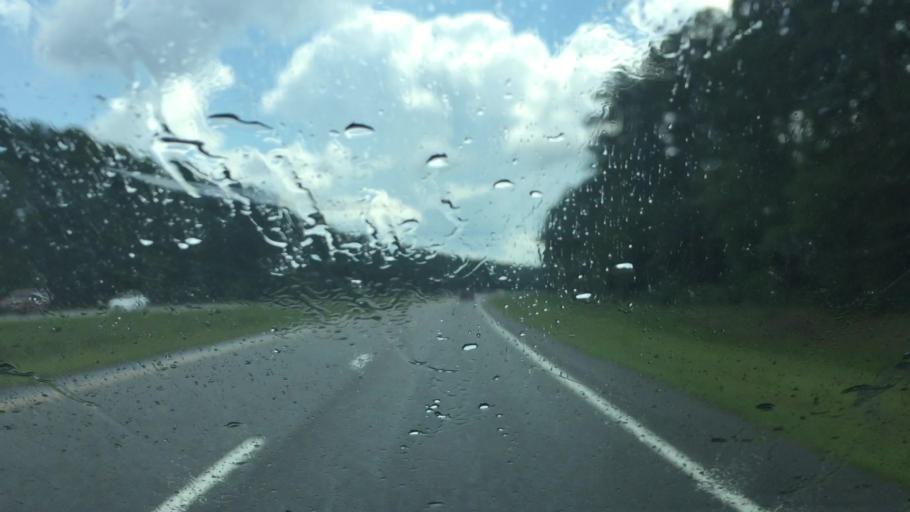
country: US
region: North Carolina
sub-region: Columbus County
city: Chadbourn
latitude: 34.3802
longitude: -78.8543
